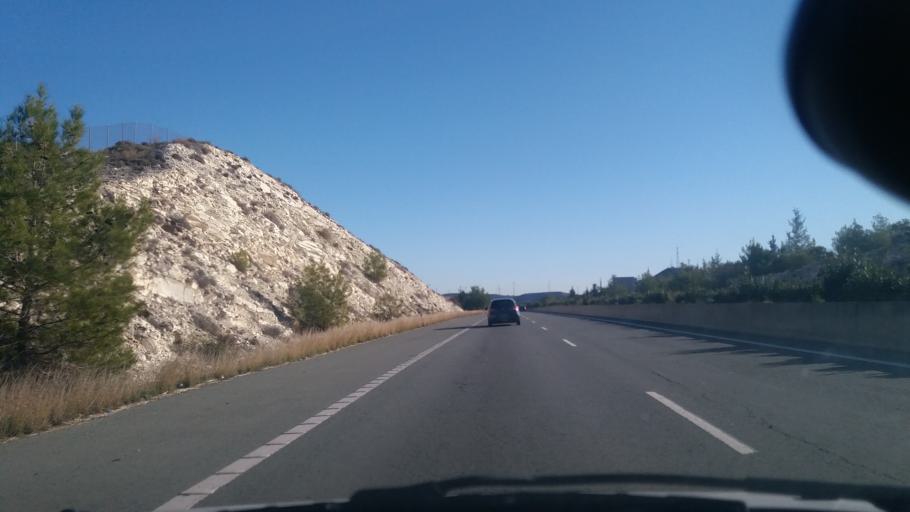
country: CY
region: Larnaka
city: Kofinou
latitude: 34.8588
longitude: 33.4608
